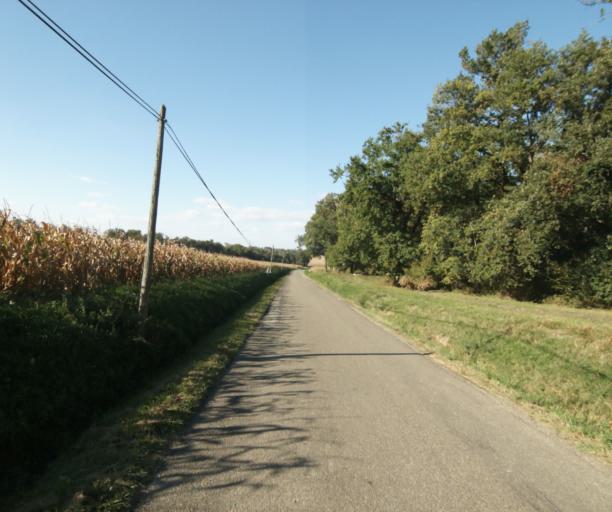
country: FR
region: Midi-Pyrenees
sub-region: Departement du Gers
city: Eauze
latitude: 43.8046
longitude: 0.1309
